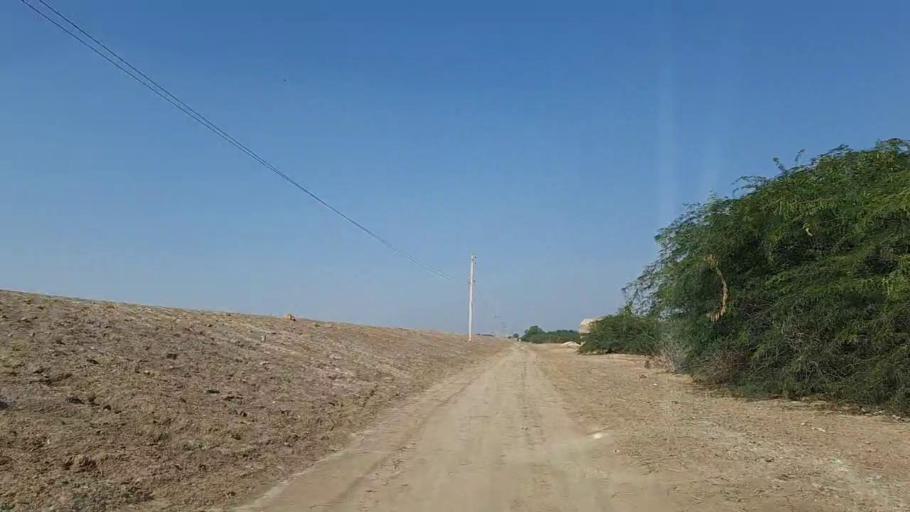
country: PK
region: Sindh
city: Chuhar Jamali
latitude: 24.5407
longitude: 68.0157
